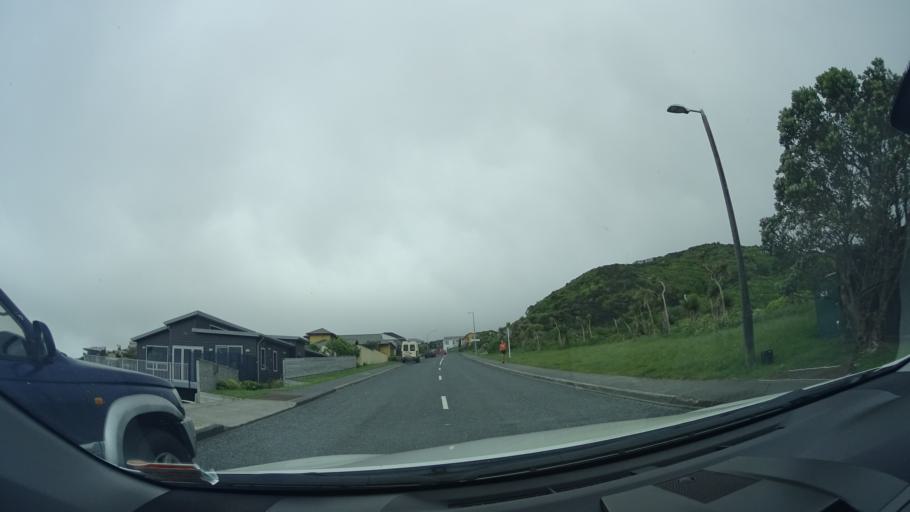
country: NZ
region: Wellington
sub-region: Wellington City
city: Brooklyn
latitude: -41.3040
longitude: 174.7543
